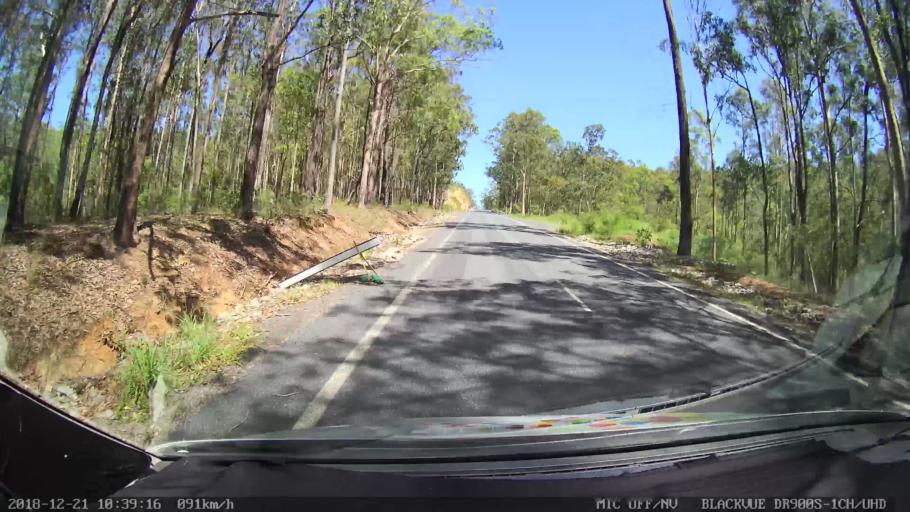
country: AU
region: New South Wales
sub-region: Clarence Valley
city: Gordon
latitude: -29.6090
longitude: 152.5989
